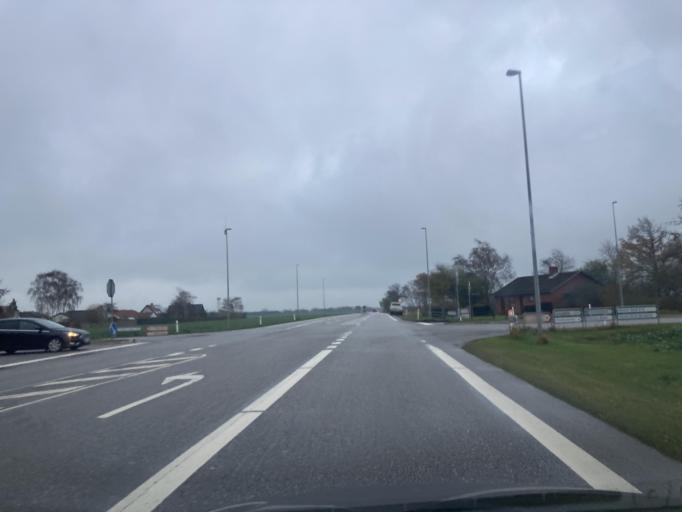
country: DK
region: Zealand
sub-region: Lolland Kommune
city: Holeby
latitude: 54.7091
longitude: 11.4557
